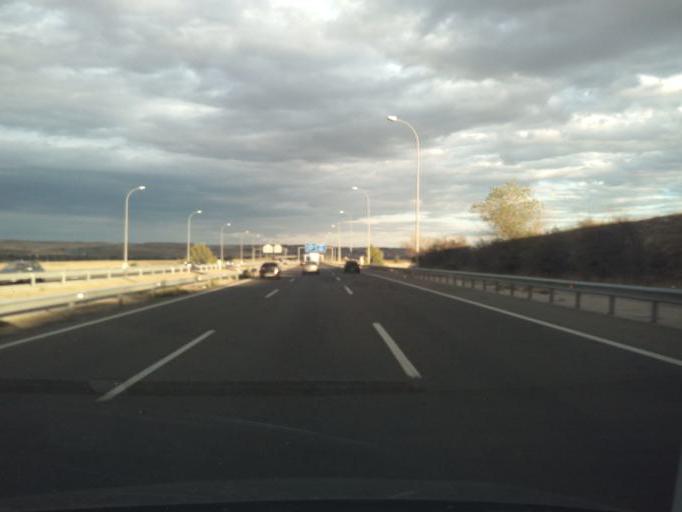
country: ES
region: Madrid
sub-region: Provincia de Madrid
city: San Sebastian de los Reyes
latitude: 40.5547
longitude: -3.5862
